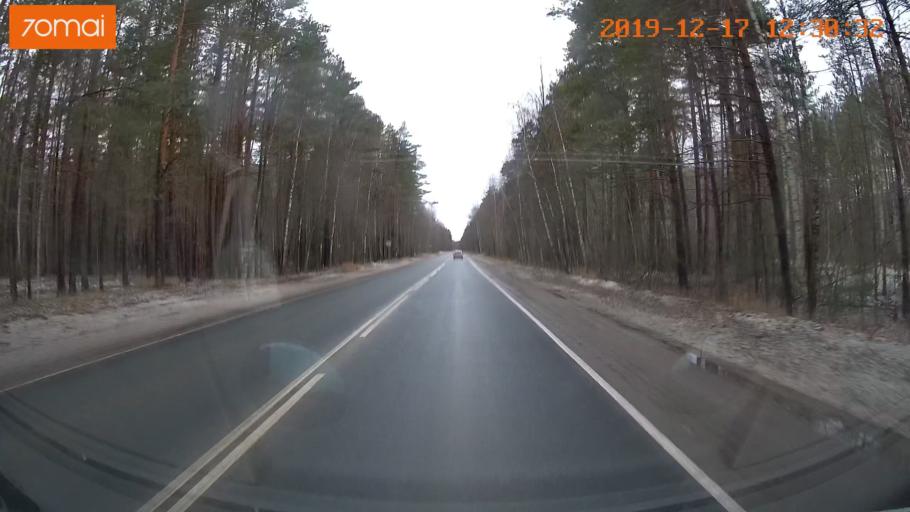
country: RU
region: Rjazan
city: Spas-Klepiki
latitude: 55.0400
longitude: 39.9984
